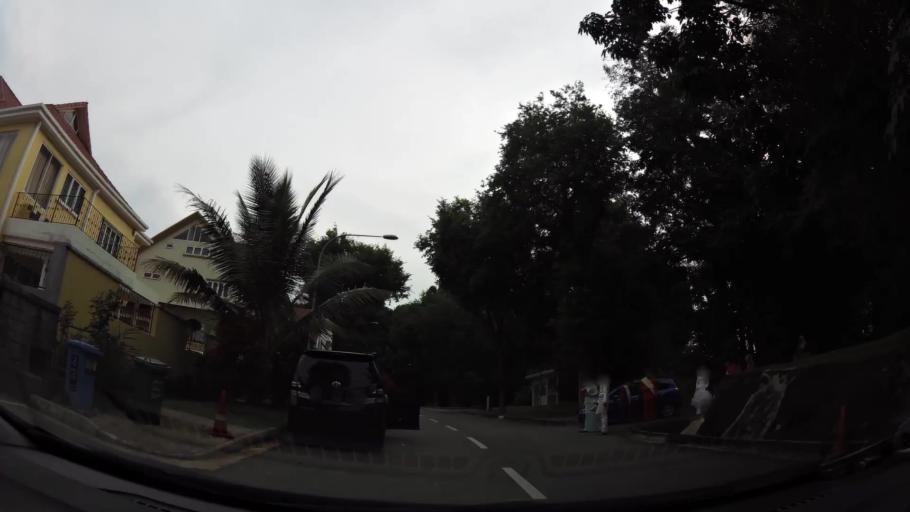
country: MY
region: Johor
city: Kampung Pasir Gudang Baru
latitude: 1.4193
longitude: 103.9084
